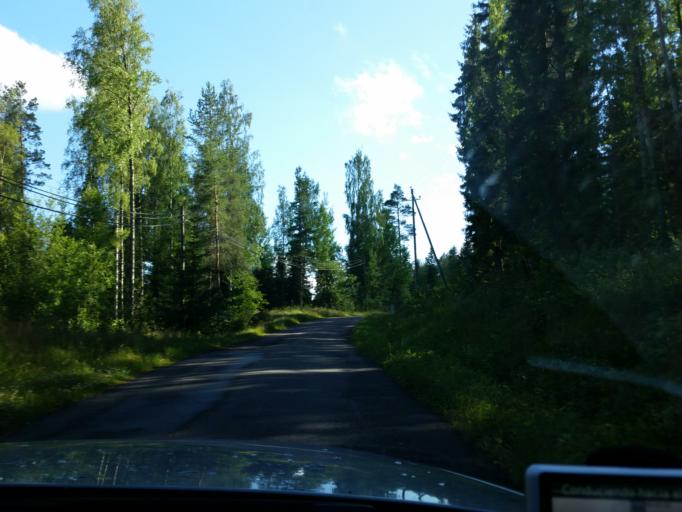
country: FI
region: Uusimaa
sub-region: Helsinki
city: Kaerkoelae
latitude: 60.5660
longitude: 24.0048
